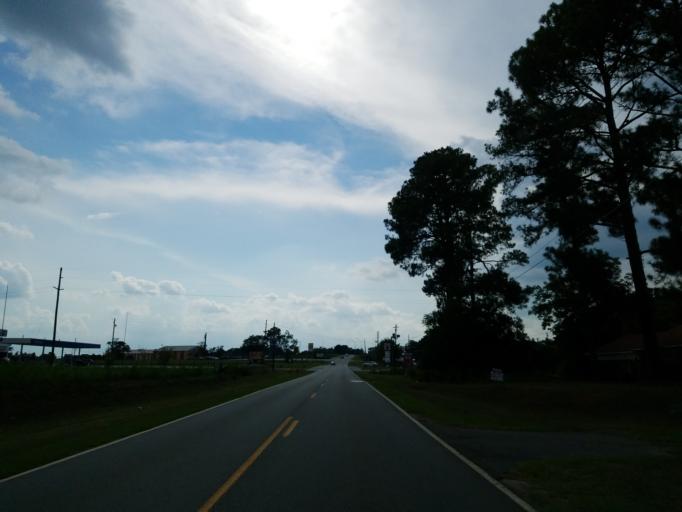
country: US
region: Georgia
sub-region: Dooly County
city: Unadilla
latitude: 32.2605
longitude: -83.7448
